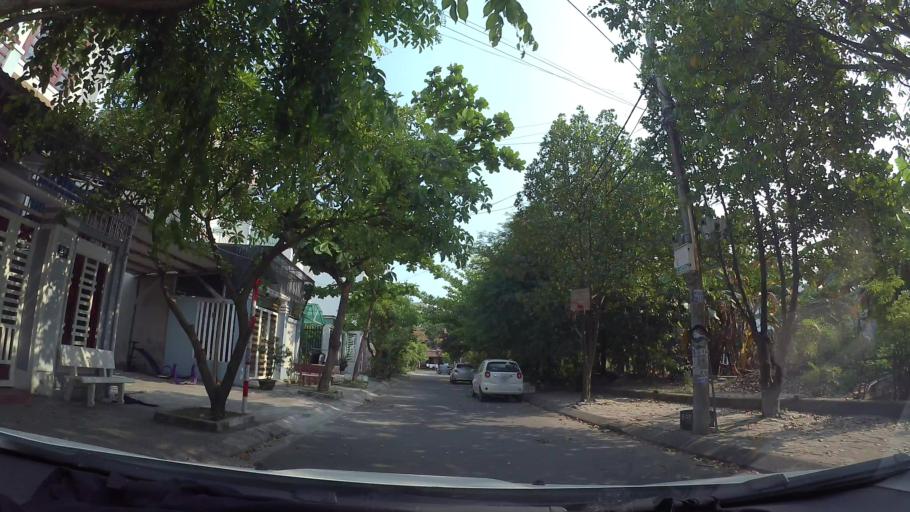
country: VN
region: Da Nang
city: Cam Le
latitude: 16.0173
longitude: 108.2016
